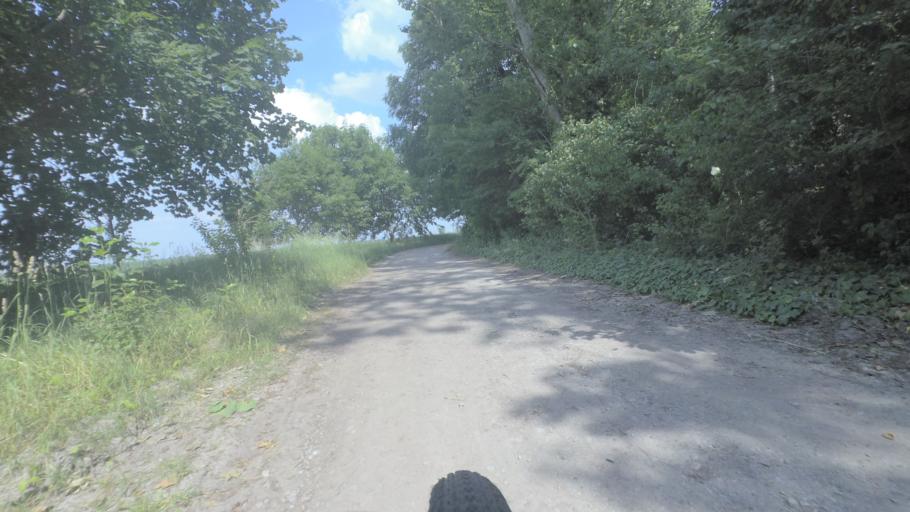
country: DE
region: Saxony-Anhalt
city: Edderitz
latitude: 51.7521
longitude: 11.9017
